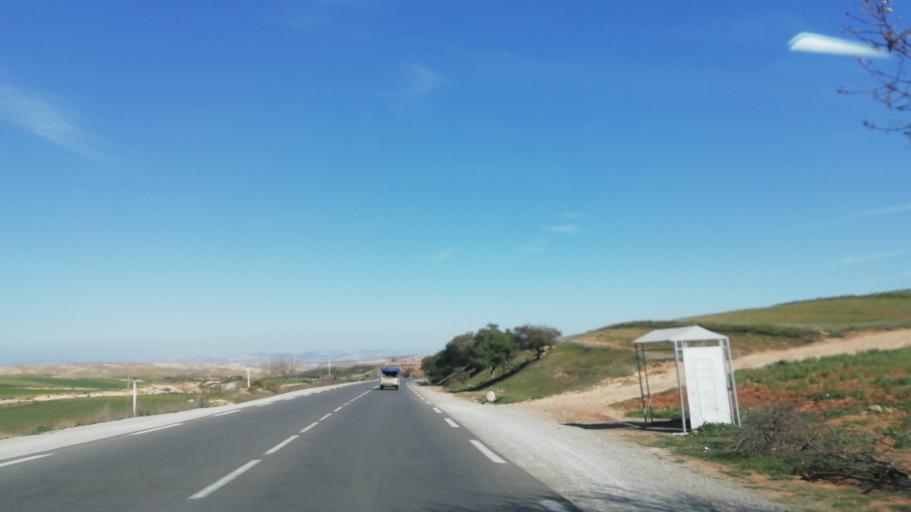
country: DZ
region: Mascara
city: Oued el Abtal
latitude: 35.4308
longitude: 0.4821
